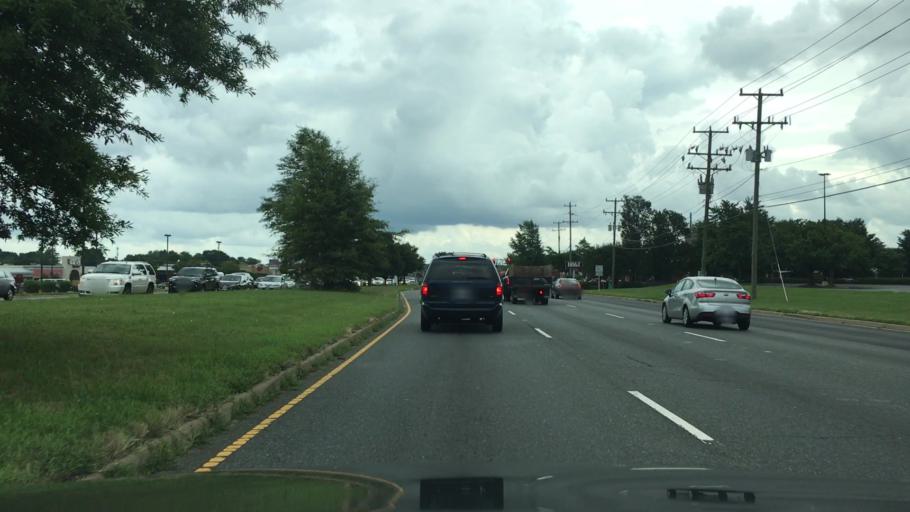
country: US
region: Virginia
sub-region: Stafford County
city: Falmouth
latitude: 38.2921
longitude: -77.5240
